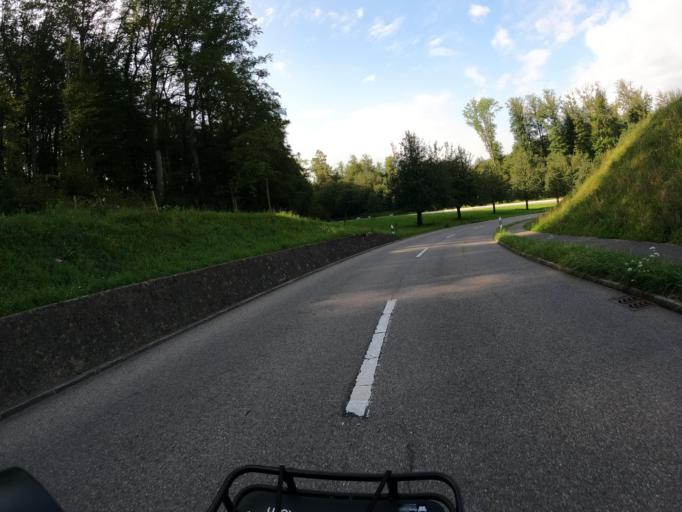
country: CH
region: Lucerne
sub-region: Hochdorf District
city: Hitzkirch
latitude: 47.2151
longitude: 8.2758
